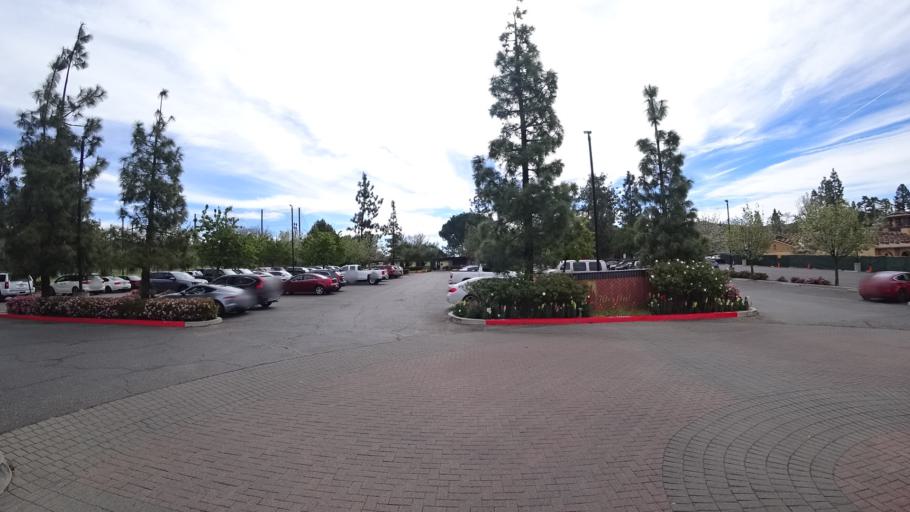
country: US
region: California
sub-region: Los Angeles County
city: Westlake Village
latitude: 34.1503
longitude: -118.8185
